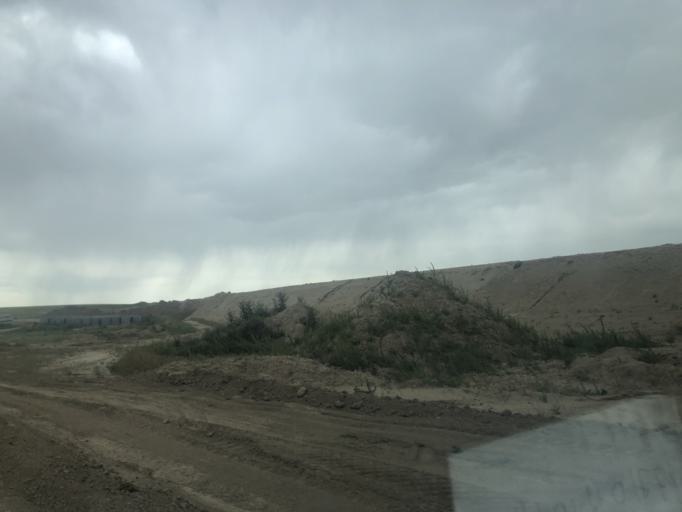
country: KG
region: Chuy
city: Bystrovka
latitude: 43.3261
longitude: 75.8463
